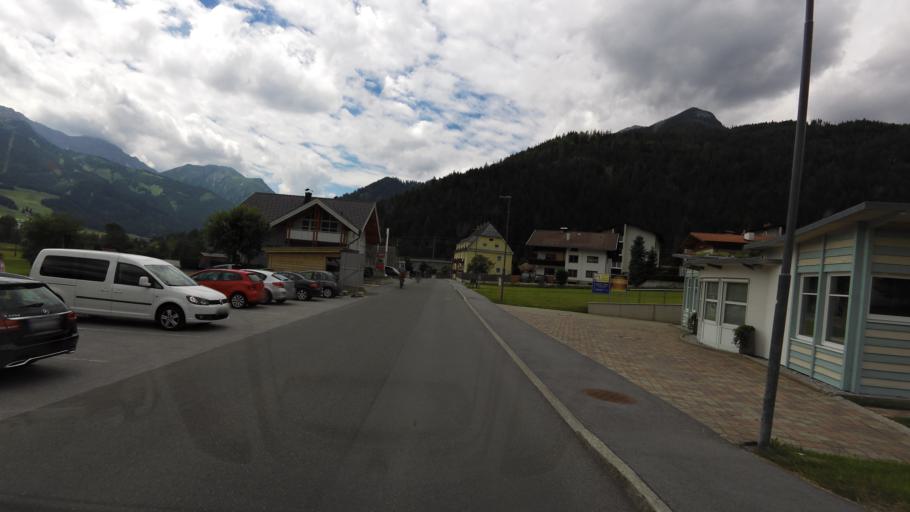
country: AT
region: Tyrol
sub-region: Politischer Bezirk Reutte
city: Ehrwald
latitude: 47.4072
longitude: 10.9147
